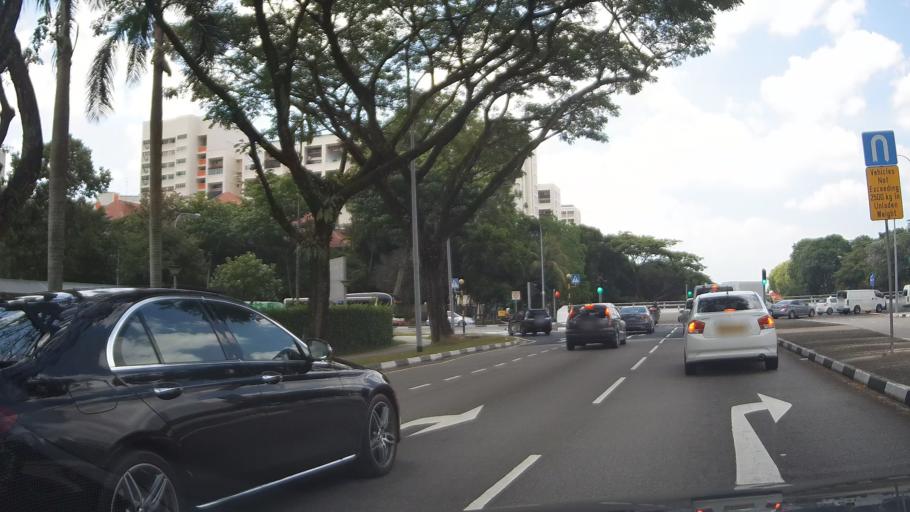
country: MY
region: Johor
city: Johor Bahru
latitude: 1.3505
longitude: 103.7283
